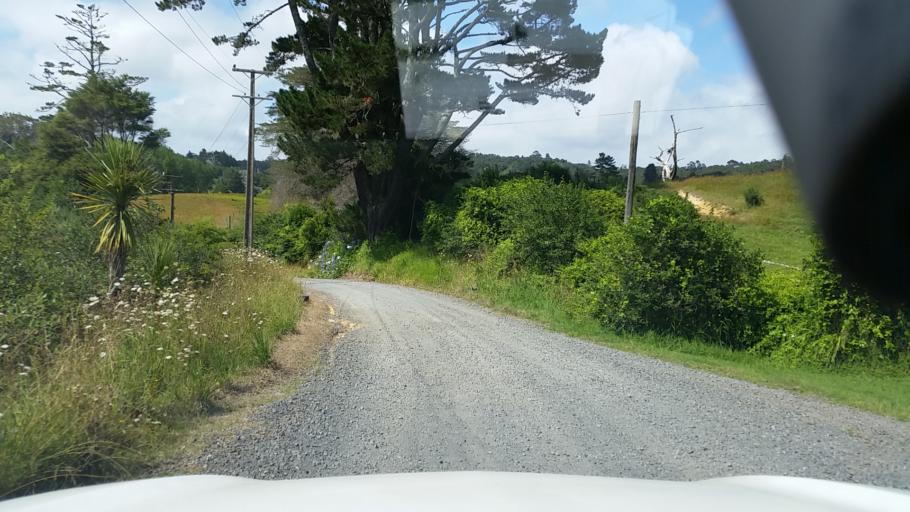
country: NZ
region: Auckland
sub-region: Auckland
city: Waitakere
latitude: -36.8771
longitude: 174.5821
